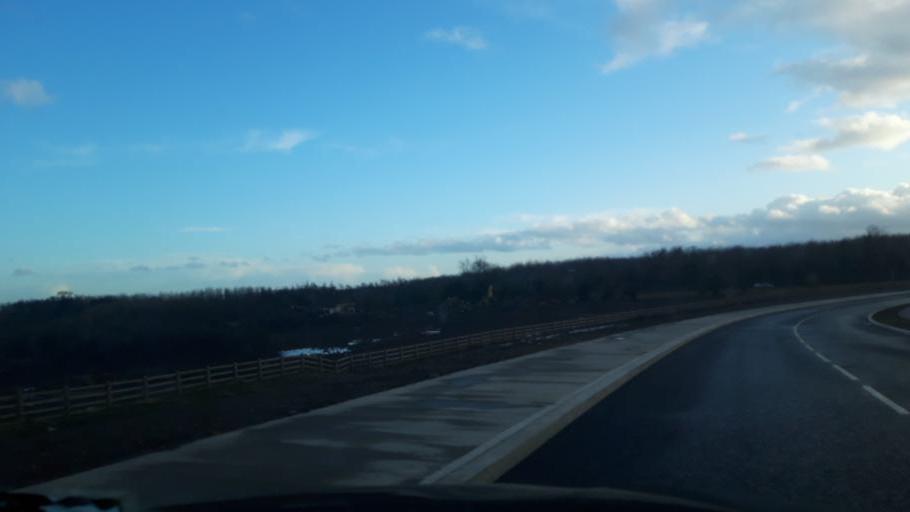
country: IE
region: Leinster
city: Donabate
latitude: 53.4805
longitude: -6.1392
